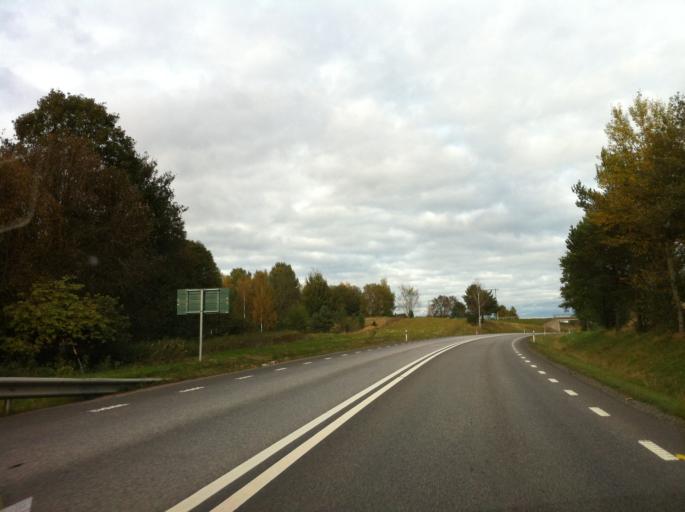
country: SE
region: OErebro
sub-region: Askersunds Kommun
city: Askersund
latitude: 58.8907
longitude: 14.9014
